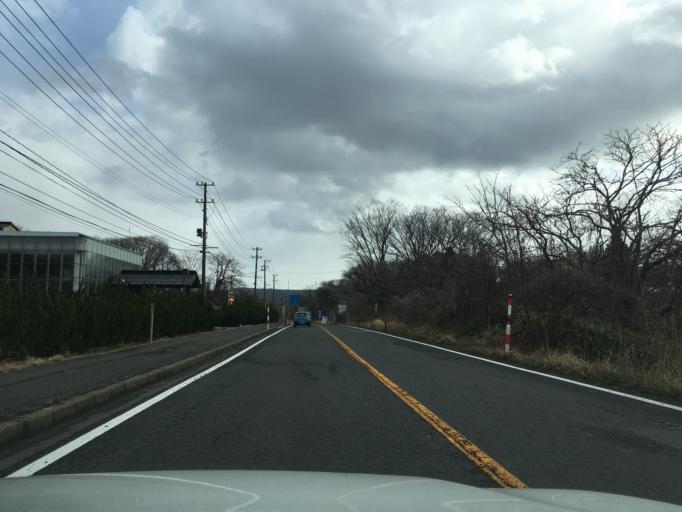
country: JP
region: Yamagata
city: Yuza
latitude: 39.2825
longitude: 139.9419
